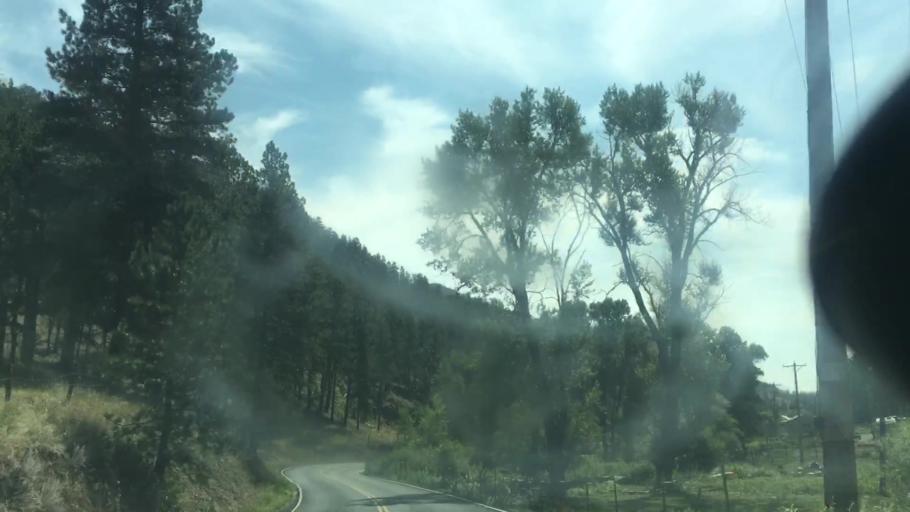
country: US
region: Colorado
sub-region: Larimer County
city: Laporte
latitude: 40.5983
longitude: -105.3402
